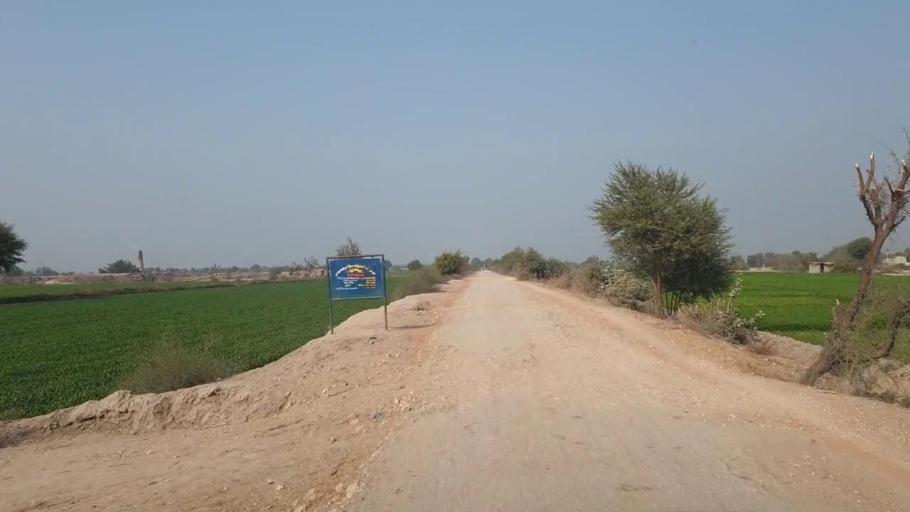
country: PK
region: Sindh
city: Hala
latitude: 25.8608
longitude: 68.4619
